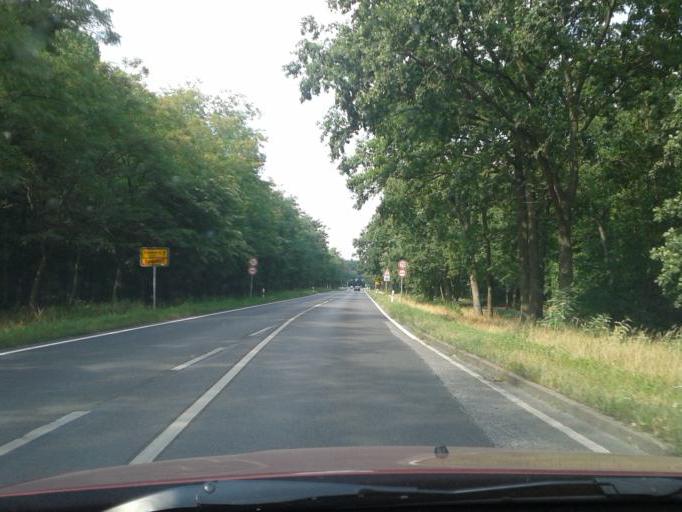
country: DE
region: Brandenburg
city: Birkenwerder
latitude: 52.7096
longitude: 13.2637
